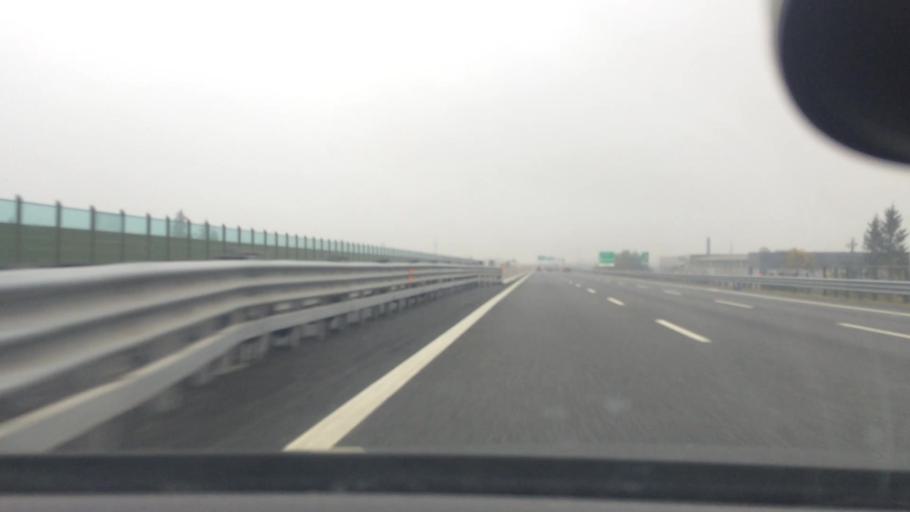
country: IT
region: Lombardy
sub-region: Provincia di Varese
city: Gerenzano
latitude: 45.6336
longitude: 9.0141
